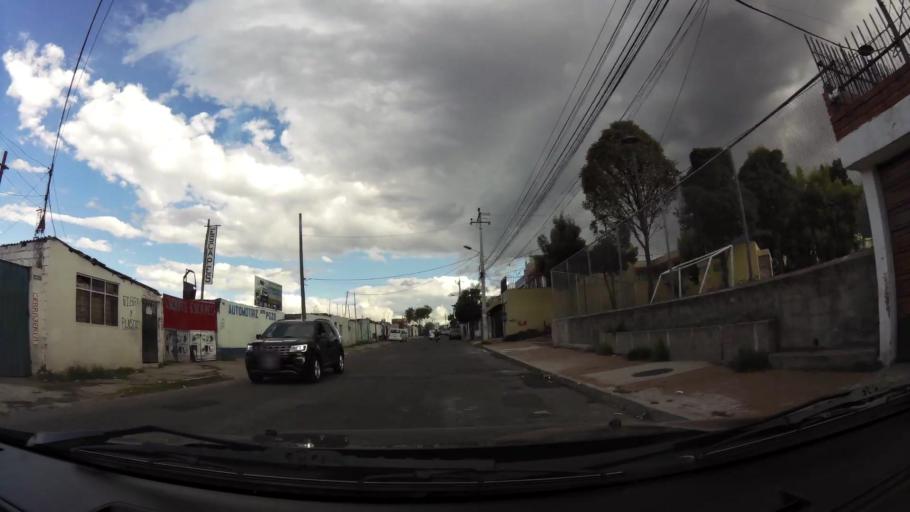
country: EC
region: Pichincha
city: Quito
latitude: -0.1251
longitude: -78.4918
